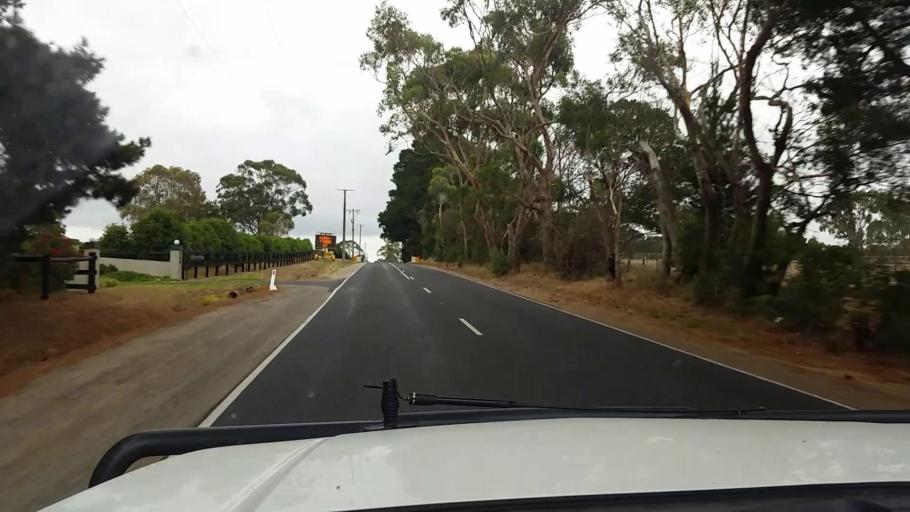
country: AU
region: Victoria
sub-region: Mornington Peninsula
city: Tyabb
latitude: -38.2631
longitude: 145.1456
